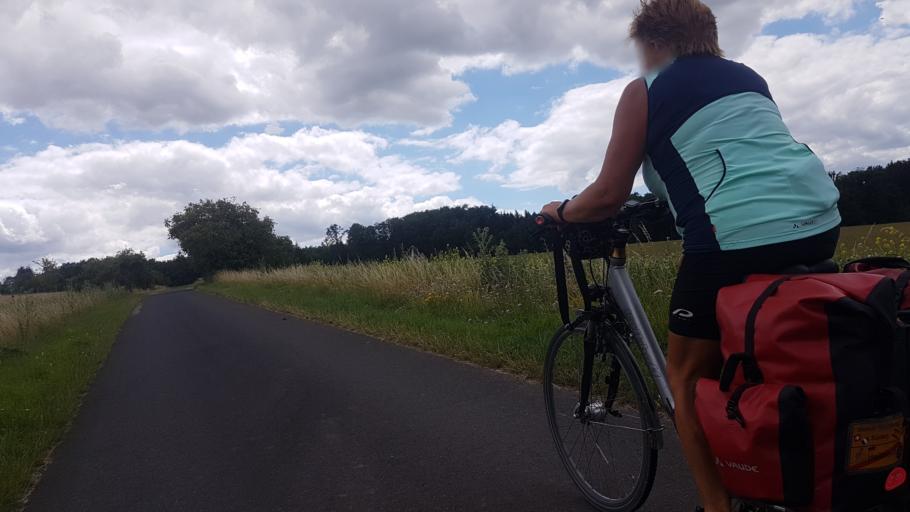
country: DE
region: Baden-Wuerttemberg
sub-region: Regierungsbezirk Stuttgart
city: Assamstadt
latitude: 49.4330
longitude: 9.7449
